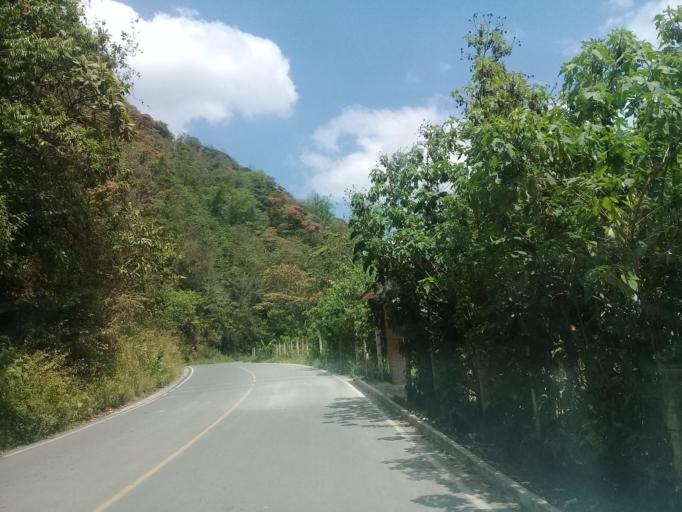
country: MX
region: Veracruz
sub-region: Tlilapan
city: Tonalixco
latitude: 18.7863
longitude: -97.0610
